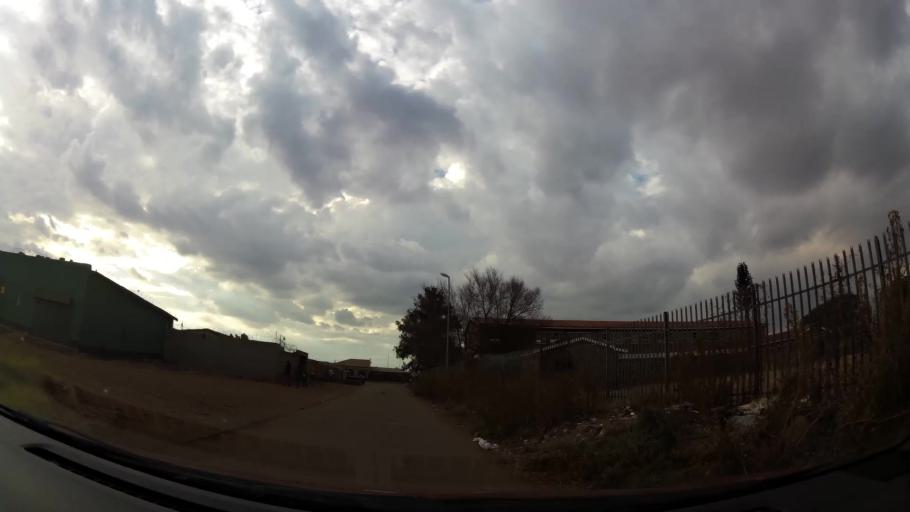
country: ZA
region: Gauteng
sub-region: City of Johannesburg Metropolitan Municipality
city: Soweto
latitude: -26.2450
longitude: 27.8164
